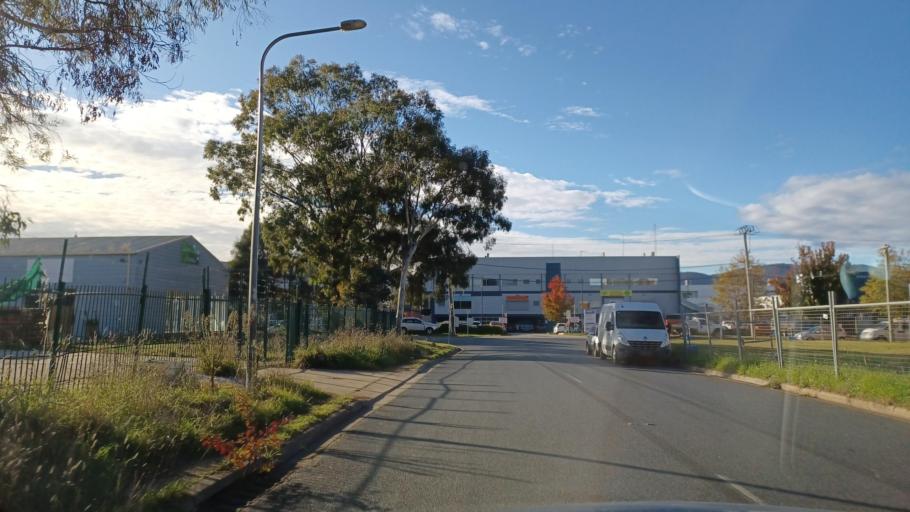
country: AU
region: Australian Capital Territory
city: Kaleen
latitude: -35.2185
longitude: 149.1431
